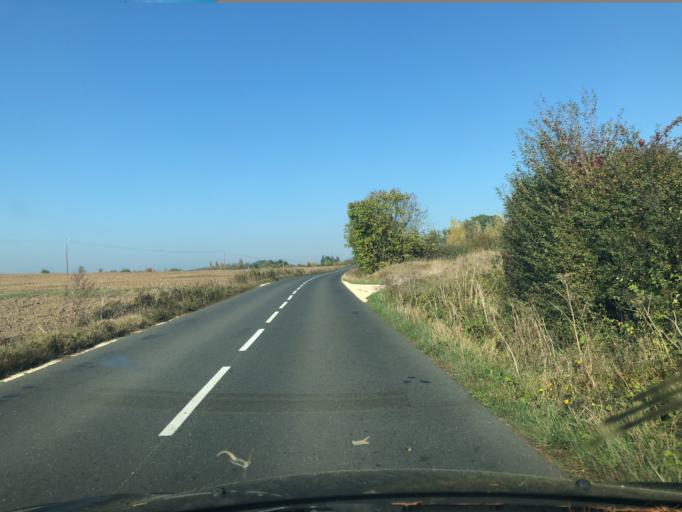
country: FR
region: Centre
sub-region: Departement d'Indre-et-Loire
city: Mettray
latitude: 47.4653
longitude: 0.6695
